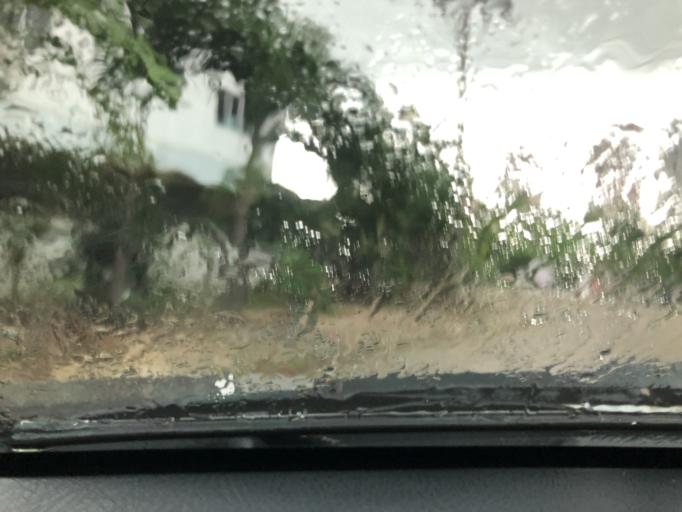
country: TH
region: Nonthaburi
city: Pak Kret
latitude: 13.9236
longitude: 100.5331
